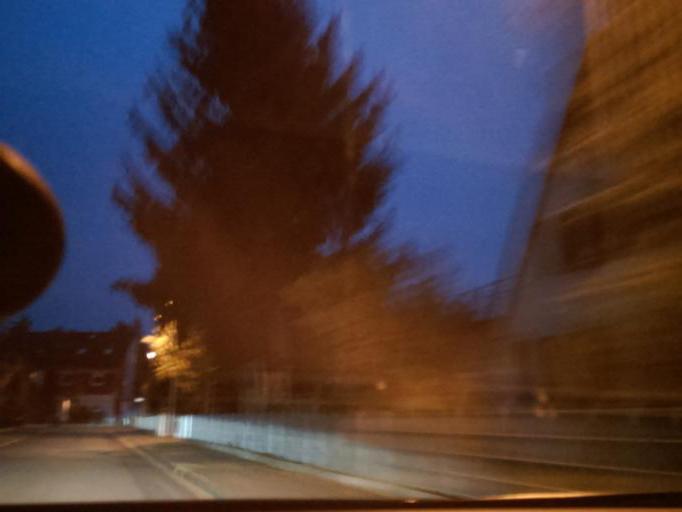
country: DE
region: Bavaria
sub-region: Regierungsbezirk Mittelfranken
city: Buckenhof
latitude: 49.5918
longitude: 11.0412
